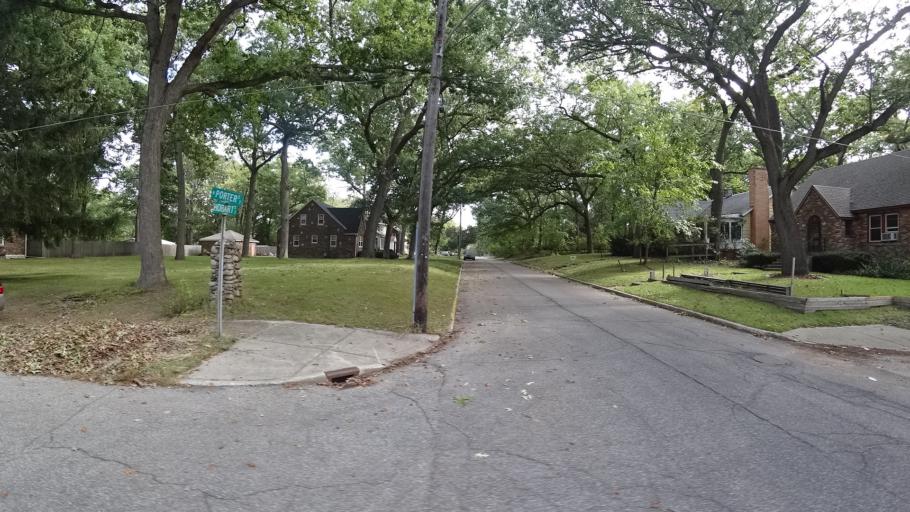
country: US
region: Indiana
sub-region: LaPorte County
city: Michigan City
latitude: 41.7153
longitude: -86.8803
